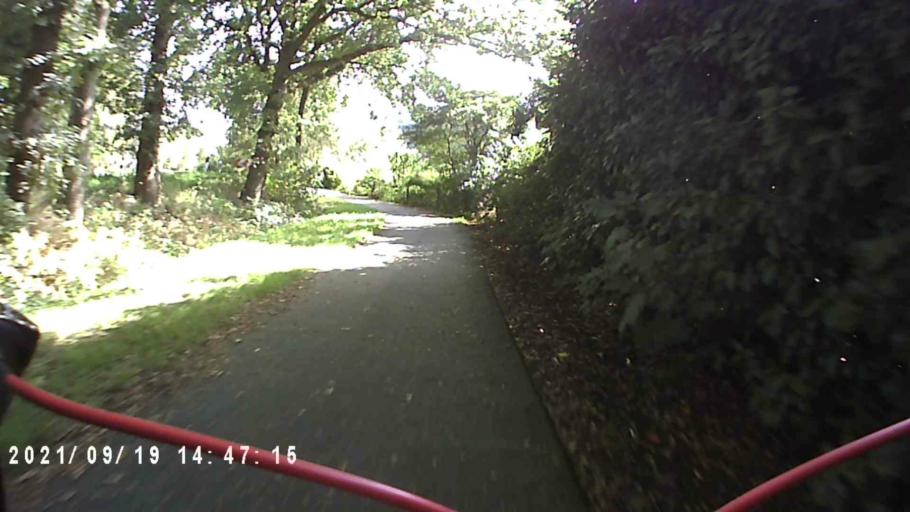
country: DE
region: Lower Saxony
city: Bunde
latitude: 53.1232
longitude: 7.1905
